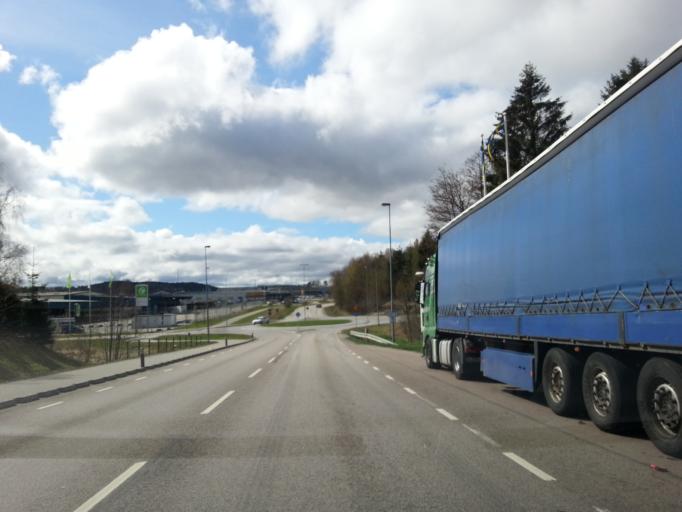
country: SE
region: Vaestra Goetaland
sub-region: Kungalvs Kommun
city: Kungalv
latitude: 57.8820
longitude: 11.9439
